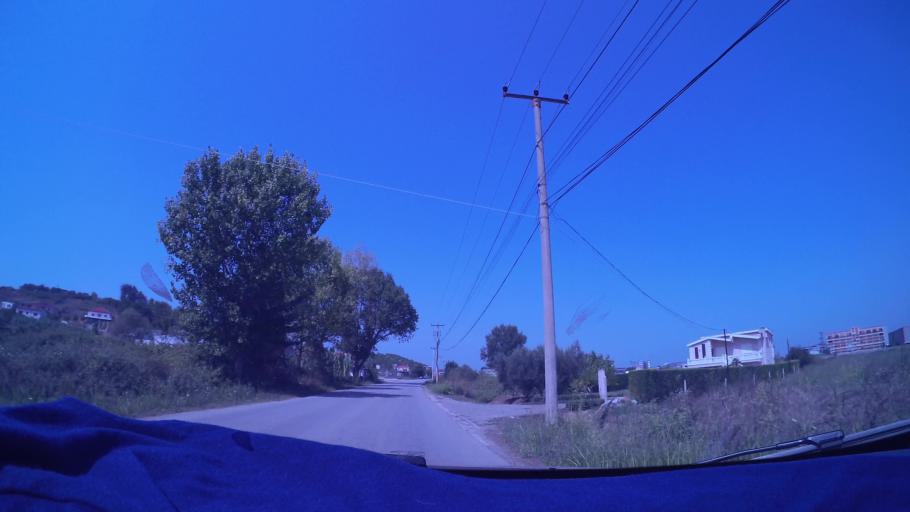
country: AL
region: Durres
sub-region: Rrethi i Durresit
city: Shijak
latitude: 41.3649
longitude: 19.5712
